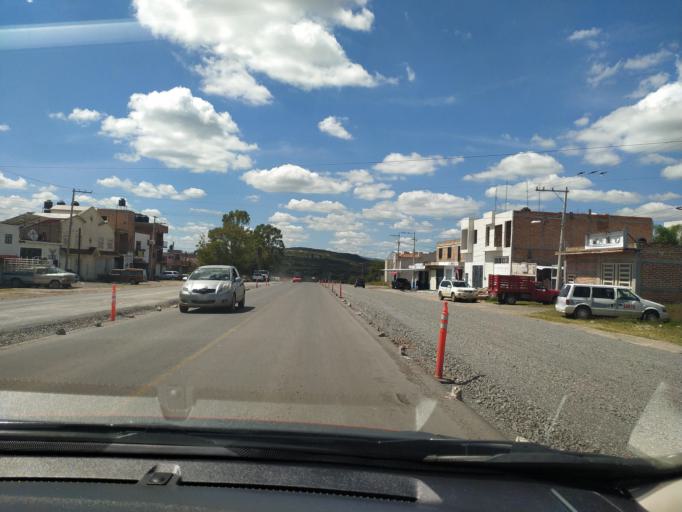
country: MX
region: Jalisco
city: San Miguel el Alto
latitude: 21.0411
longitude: -102.4023
